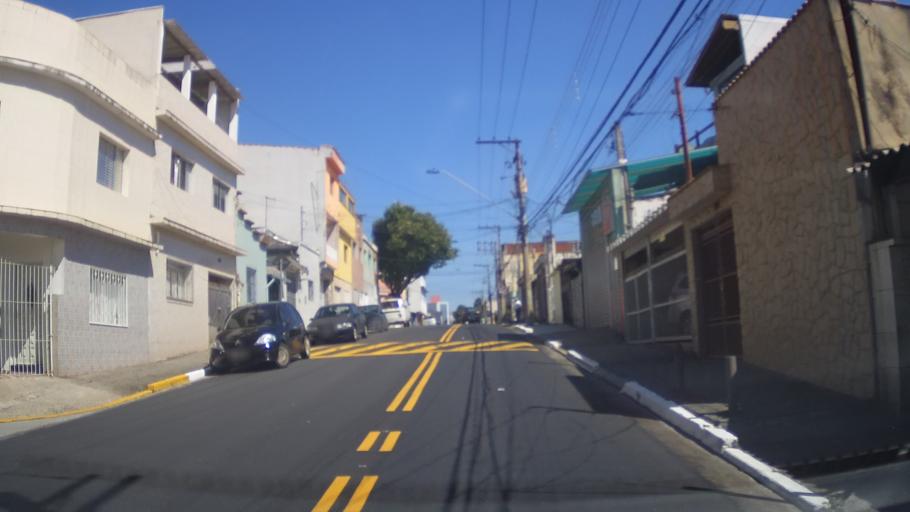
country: BR
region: Sao Paulo
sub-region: Sao Caetano Do Sul
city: Sao Caetano do Sul
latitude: -23.6386
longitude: -46.5625
